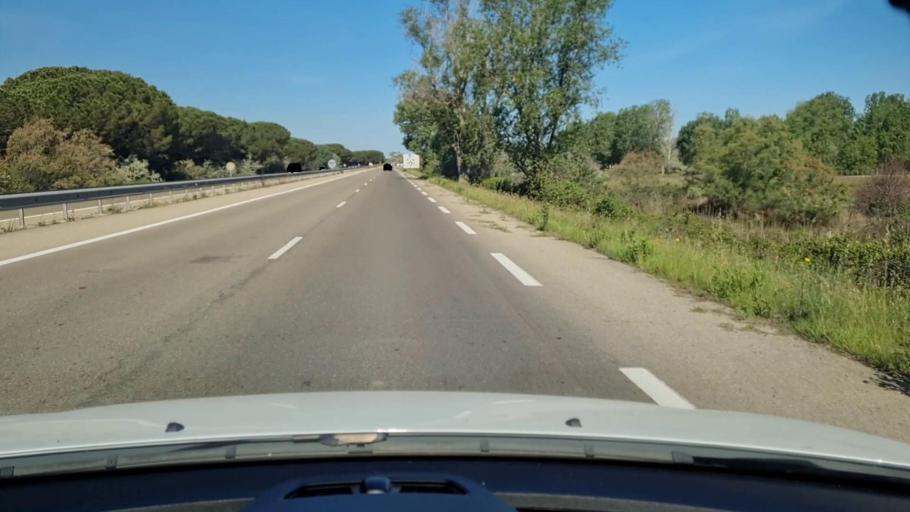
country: FR
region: Languedoc-Roussillon
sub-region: Departement du Gard
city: Le Grau-du-Roi
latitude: 43.5647
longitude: 4.1295
